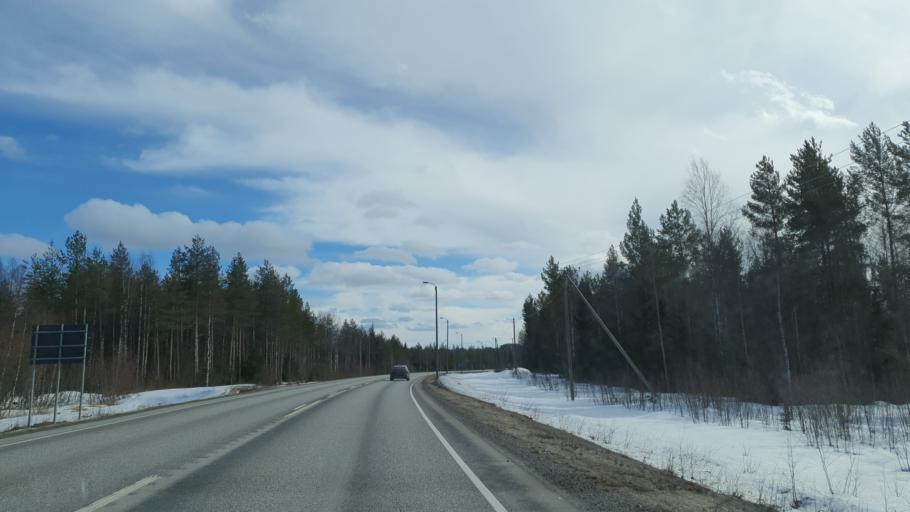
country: FI
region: Kainuu
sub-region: Kajaani
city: Paltamo
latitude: 64.3819
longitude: 28.0173
